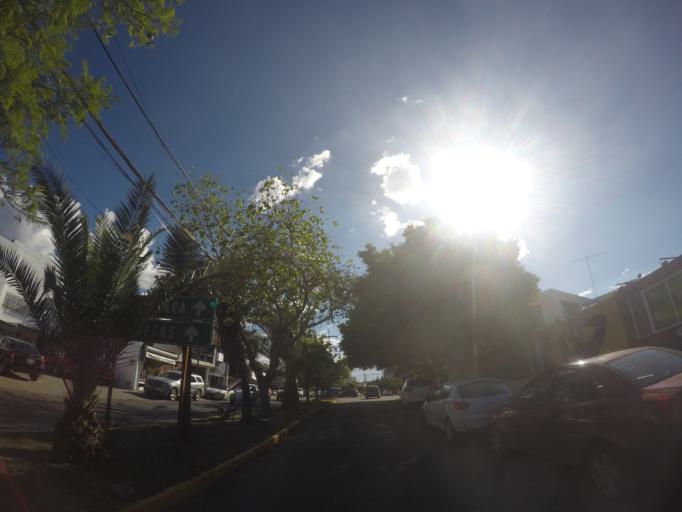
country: MX
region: San Luis Potosi
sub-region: San Luis Potosi
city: San Luis Potosi
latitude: 22.1445
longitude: -101.0209
